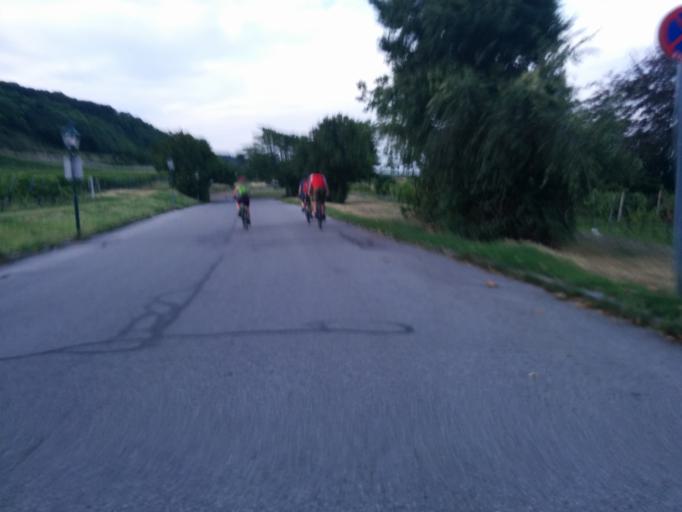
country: AT
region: Lower Austria
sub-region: Politischer Bezirk Modling
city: Gumpoldskirchen
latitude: 48.0476
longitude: 16.2776
